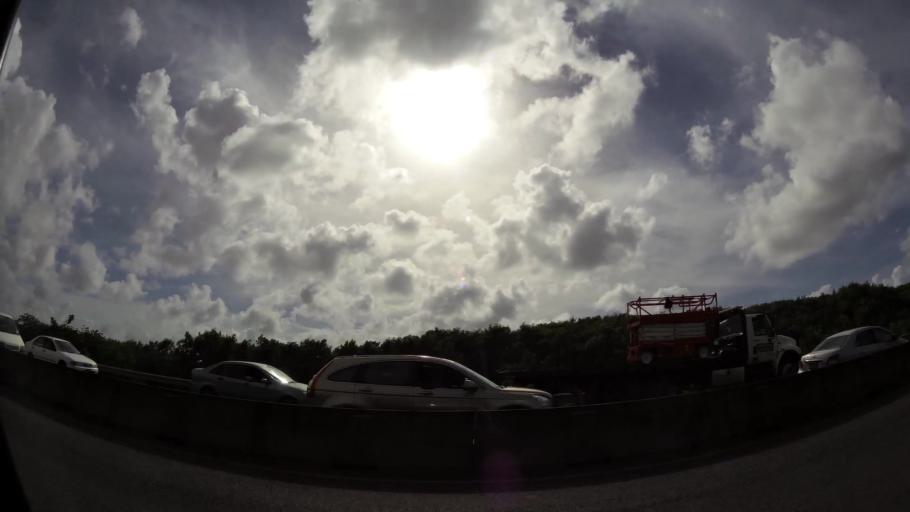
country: BB
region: Saint Michael
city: Bridgetown
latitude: 13.1316
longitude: -59.5997
